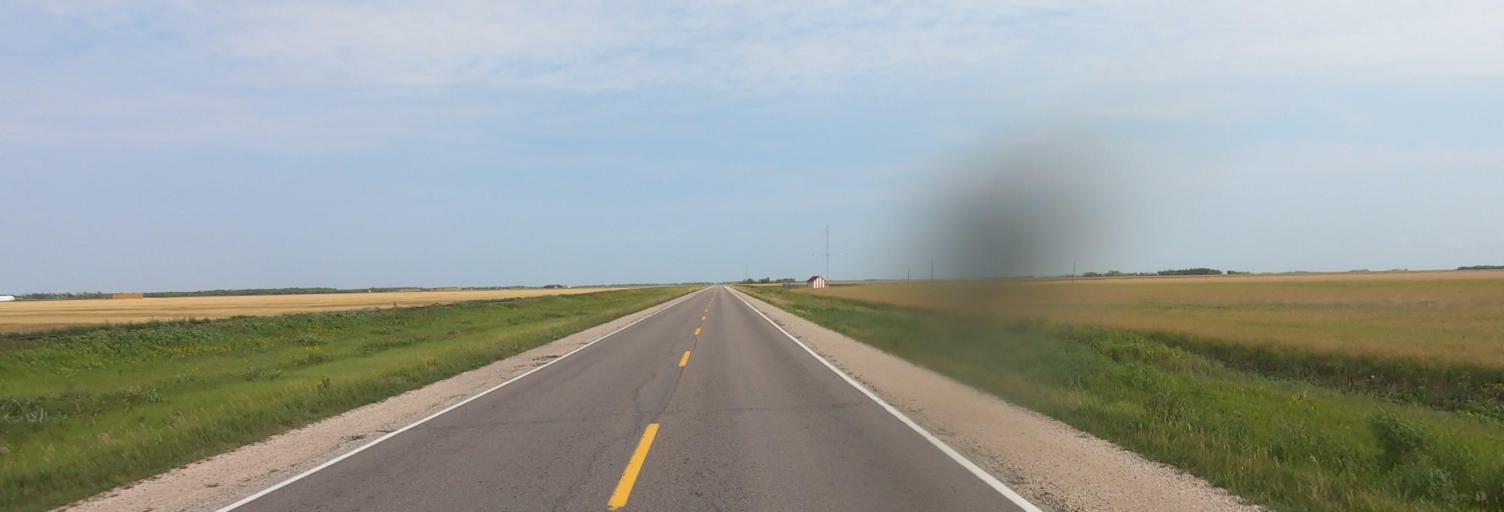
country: CA
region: Manitoba
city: Headingley
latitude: 49.6400
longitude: -97.3024
